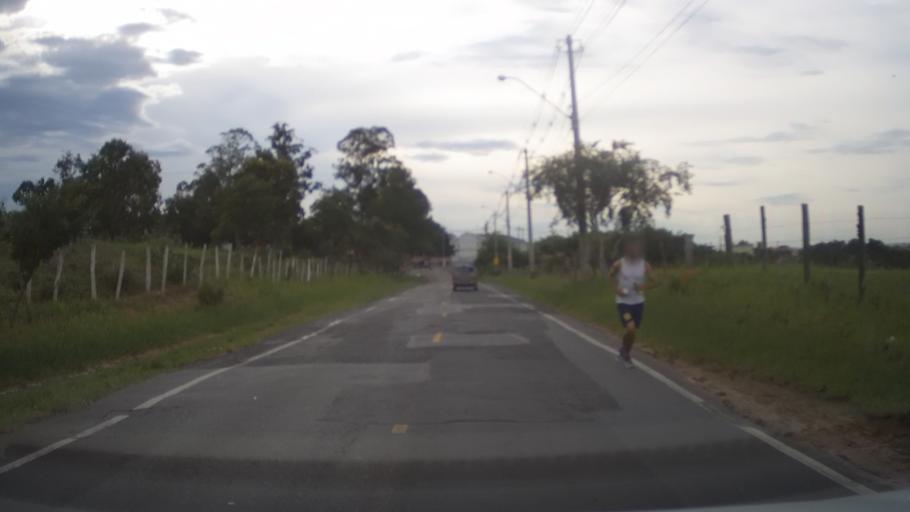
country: BR
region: Sao Paulo
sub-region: Hortolandia
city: Hortolandia
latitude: -22.9569
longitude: -47.2128
